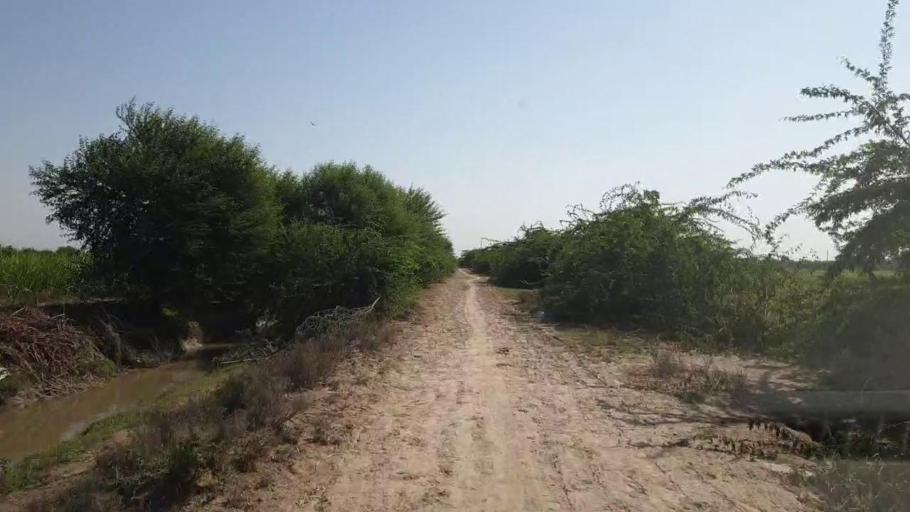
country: PK
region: Sindh
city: Kadhan
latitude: 24.5879
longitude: 69.0095
